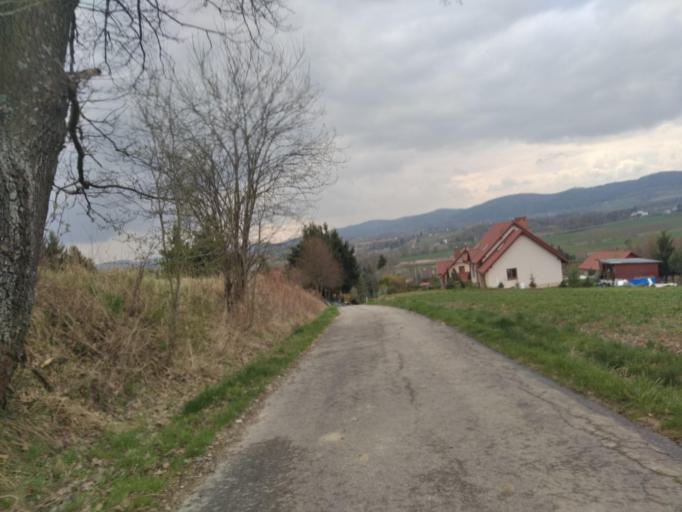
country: PL
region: Subcarpathian Voivodeship
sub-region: Powiat strzyzowski
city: Wysoka Strzyzowska
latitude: 49.8819
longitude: 21.7186
